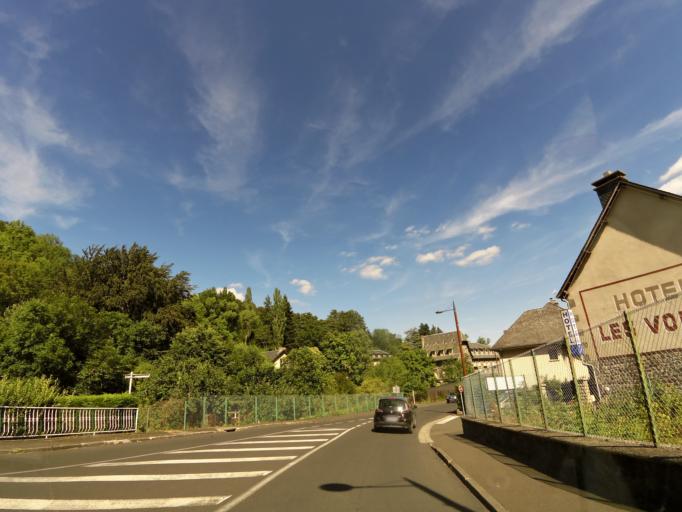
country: FR
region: Auvergne
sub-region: Departement du Puy-de-Dome
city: Aydat
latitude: 45.5746
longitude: 2.9394
